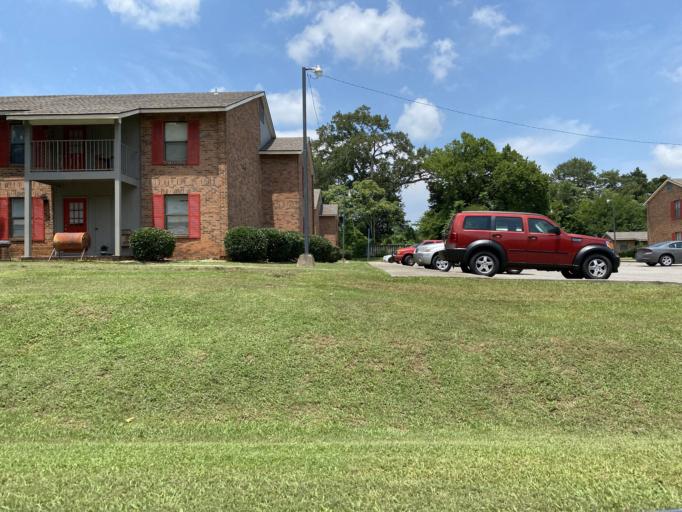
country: US
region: Alabama
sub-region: Lawrence County
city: Town Creek
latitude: 34.6691
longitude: -87.3046
